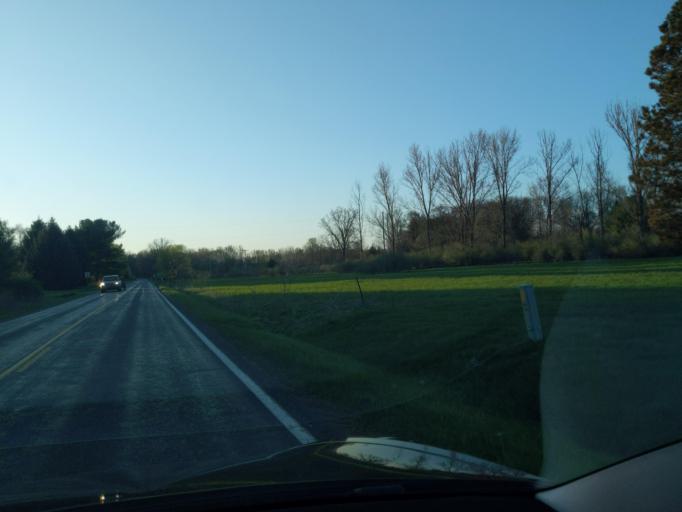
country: US
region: Michigan
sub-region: Ingham County
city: Stockbridge
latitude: 42.4809
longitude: -84.2115
